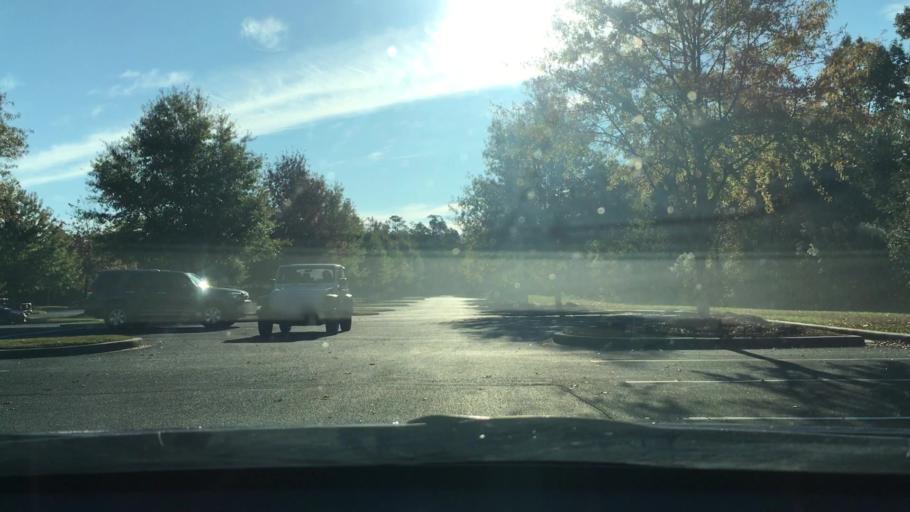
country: US
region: South Carolina
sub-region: Lexington County
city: Irmo
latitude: 34.0846
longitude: -81.1535
